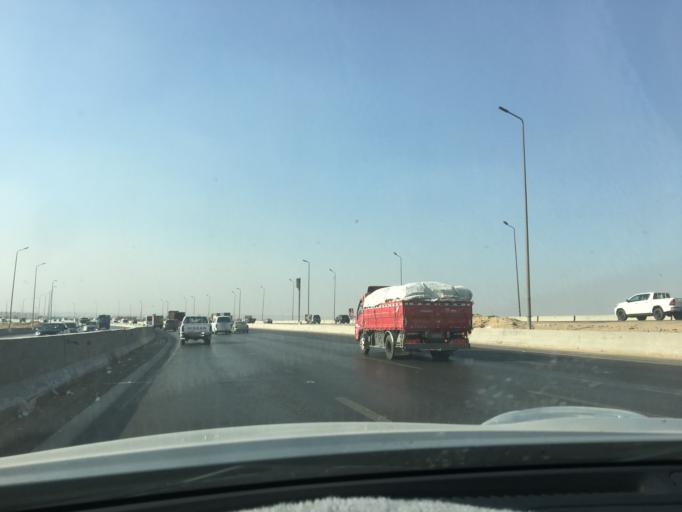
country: EG
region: Muhafazat al Qalyubiyah
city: Al Khankah
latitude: 30.1264
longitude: 31.4652
